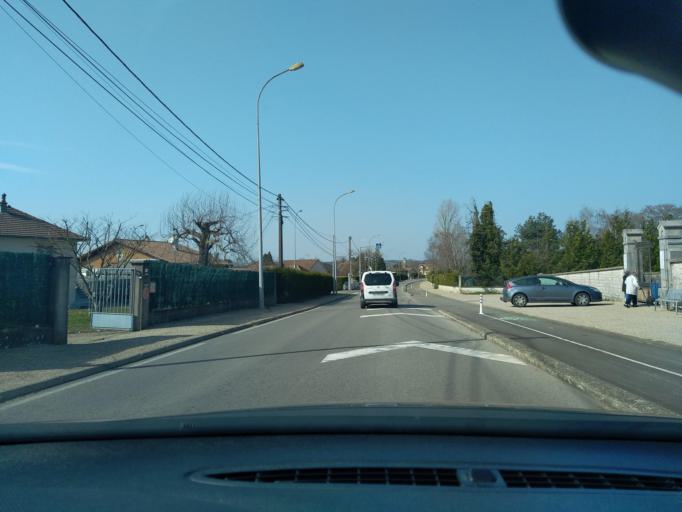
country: FR
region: Franche-Comte
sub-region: Departement du Jura
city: Dole
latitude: 47.0716
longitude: 5.5030
